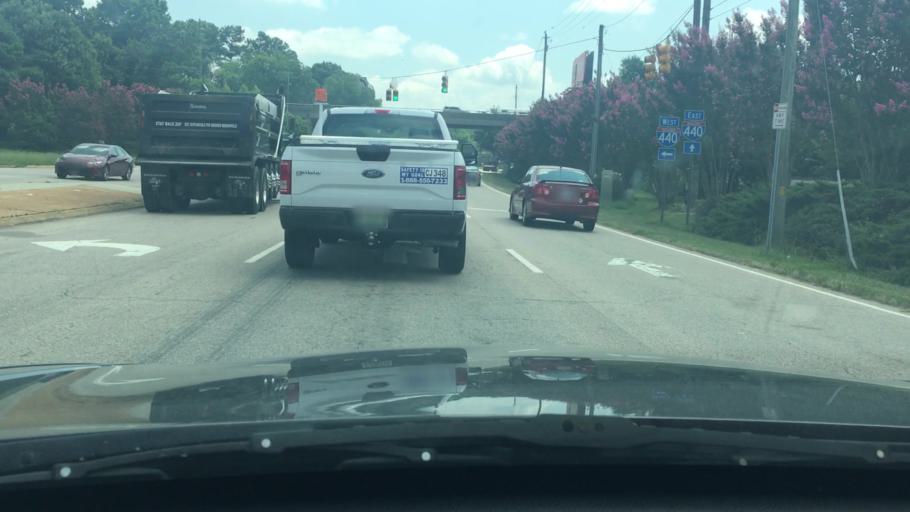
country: US
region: North Carolina
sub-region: Wake County
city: West Raleigh
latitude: 35.7957
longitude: -78.6967
